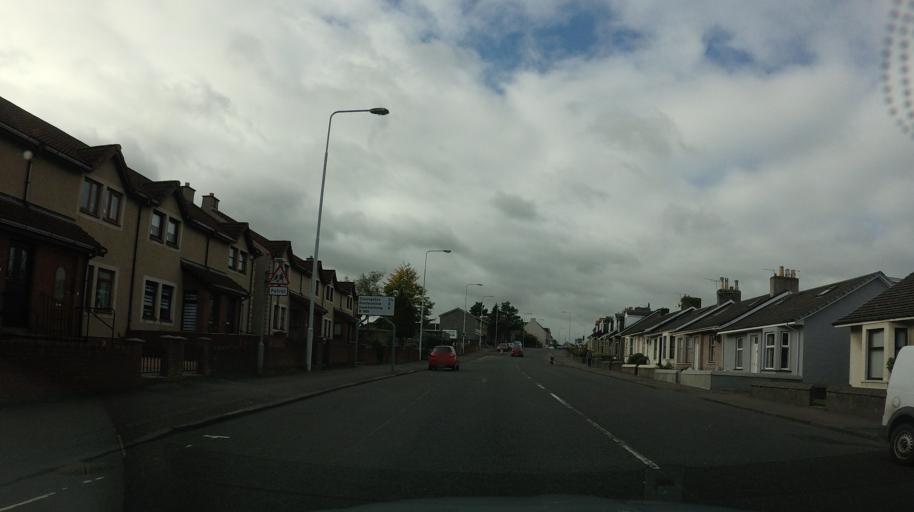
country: GB
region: Scotland
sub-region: Fife
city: Cowdenbeath
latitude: 56.1071
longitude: -3.3440
